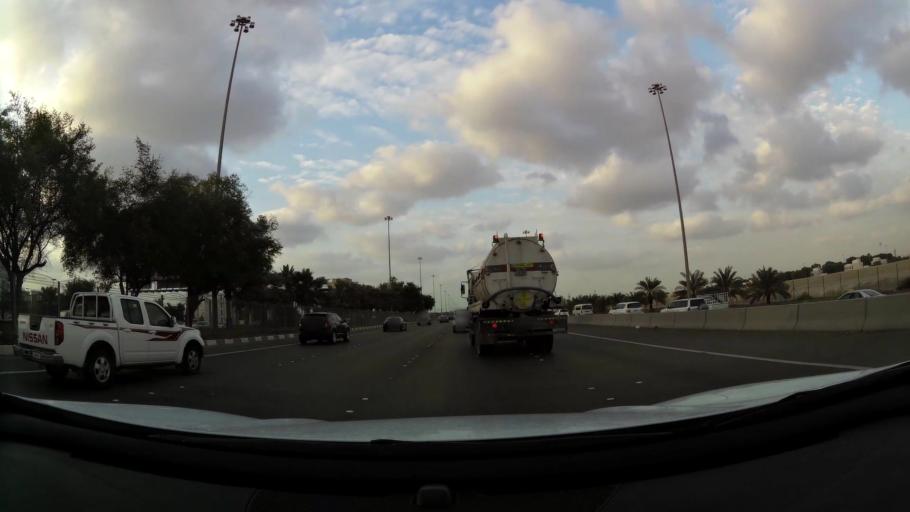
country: AE
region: Abu Dhabi
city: Abu Dhabi
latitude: 24.3775
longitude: 54.5248
